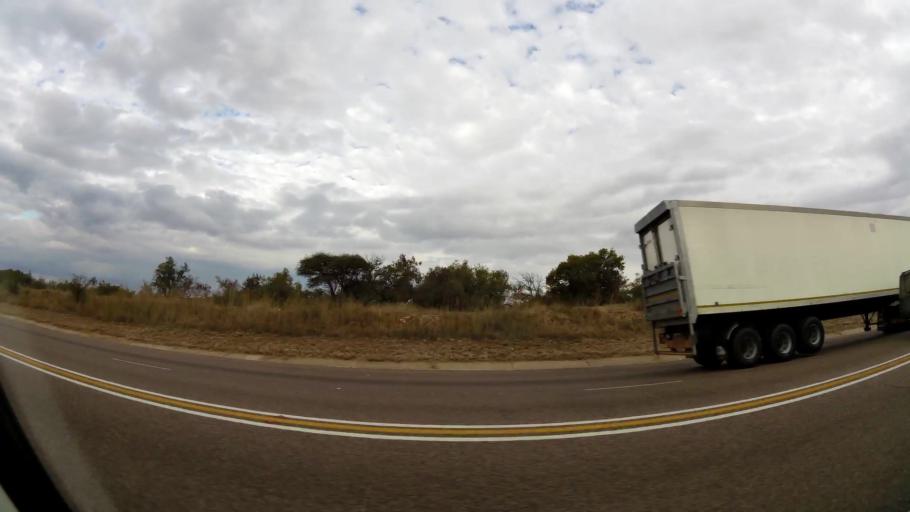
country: ZA
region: Limpopo
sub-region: Waterberg District Municipality
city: Modimolle
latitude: -24.6222
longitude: 28.6222
